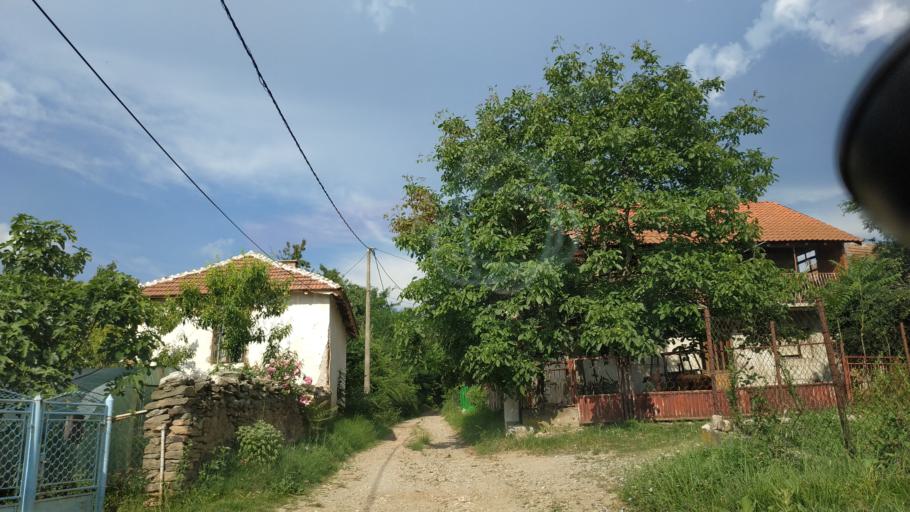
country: RS
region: Central Serbia
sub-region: Nisavski Okrug
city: Aleksinac
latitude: 43.6042
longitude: 21.6886
